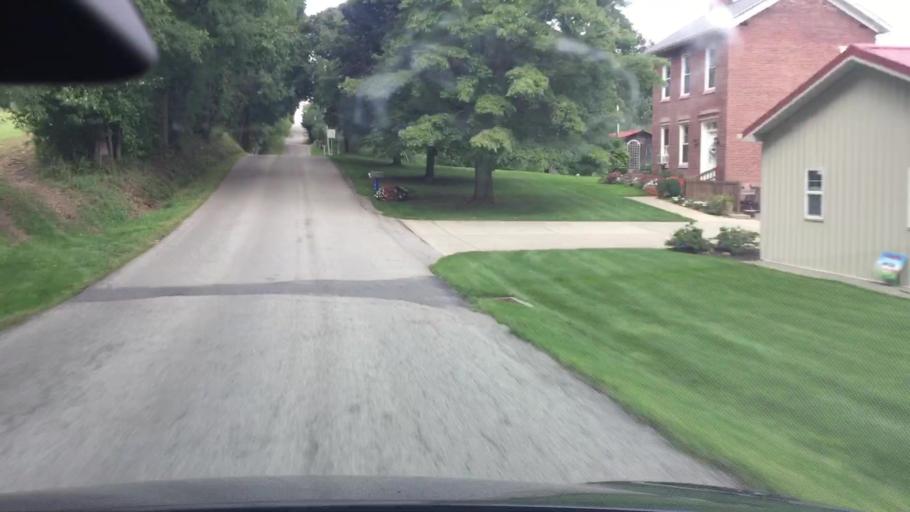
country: US
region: Pennsylvania
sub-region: Butler County
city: Nixon
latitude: 40.7621
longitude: -79.8853
